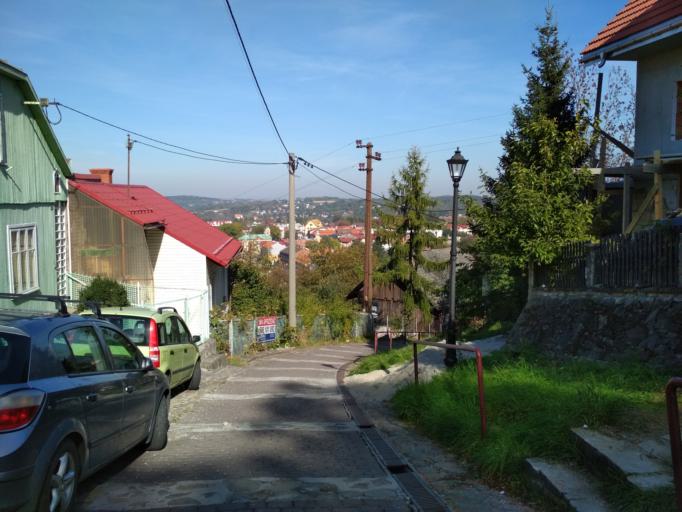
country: PL
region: Lesser Poland Voivodeship
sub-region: Powiat wadowicki
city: Kalwaria Zebrzydowska
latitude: 49.8623
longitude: 19.6747
